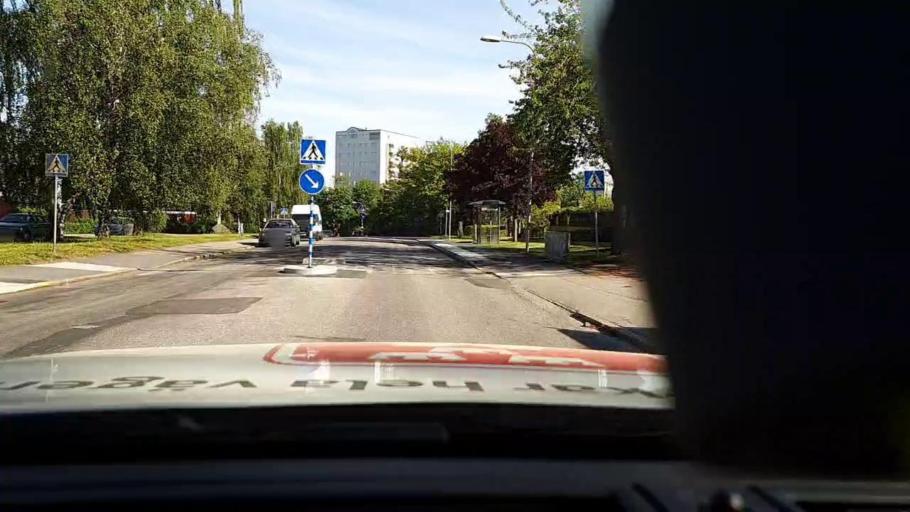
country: SE
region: Stockholm
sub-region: Stockholms Kommun
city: Arsta
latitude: 59.2663
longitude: 18.0325
